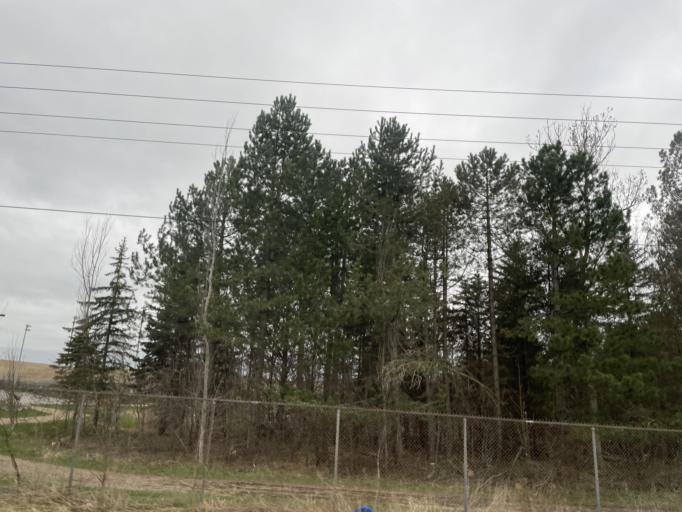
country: CA
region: Ontario
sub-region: Wellington County
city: Guelph
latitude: 43.5836
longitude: -80.2320
